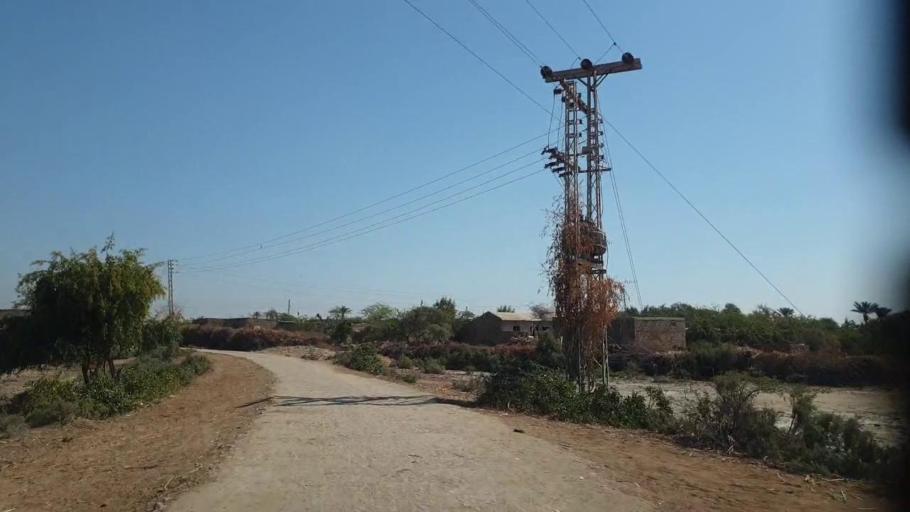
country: PK
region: Sindh
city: Mirpur Khas
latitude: 25.5823
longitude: 69.1133
